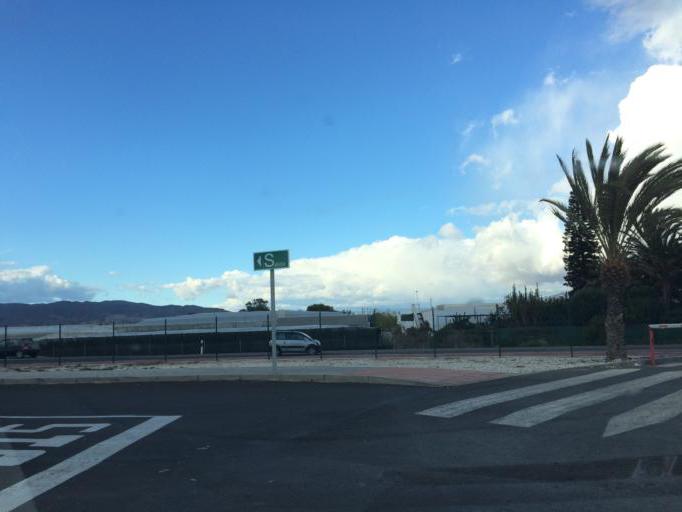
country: ES
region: Andalusia
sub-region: Provincia de Almeria
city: Almeria
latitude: 36.8301
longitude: -2.4088
